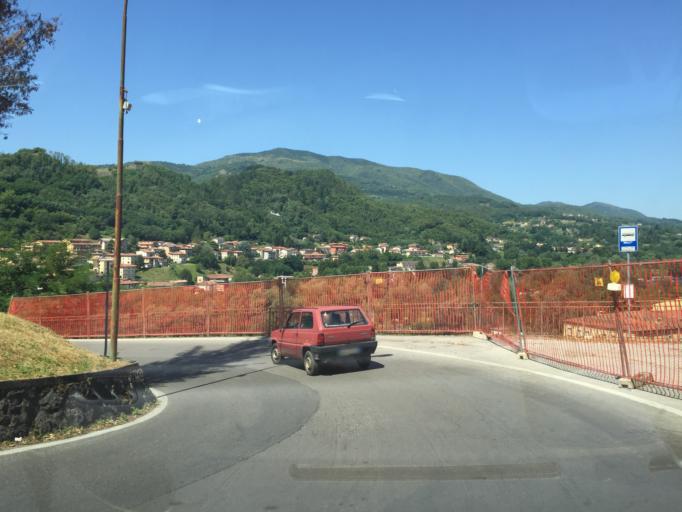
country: IT
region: Tuscany
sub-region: Provincia di Lucca
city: Castelnuovo di Garfagnana
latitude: 44.1118
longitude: 10.4142
